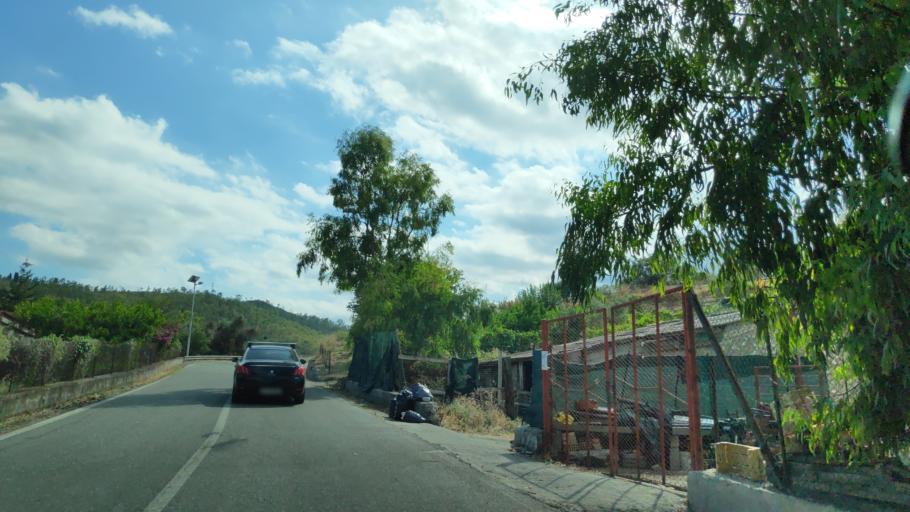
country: IT
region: Calabria
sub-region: Provincia di Catanzaro
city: Santa Caterina dello Ionio Marina
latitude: 38.5282
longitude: 16.5522
